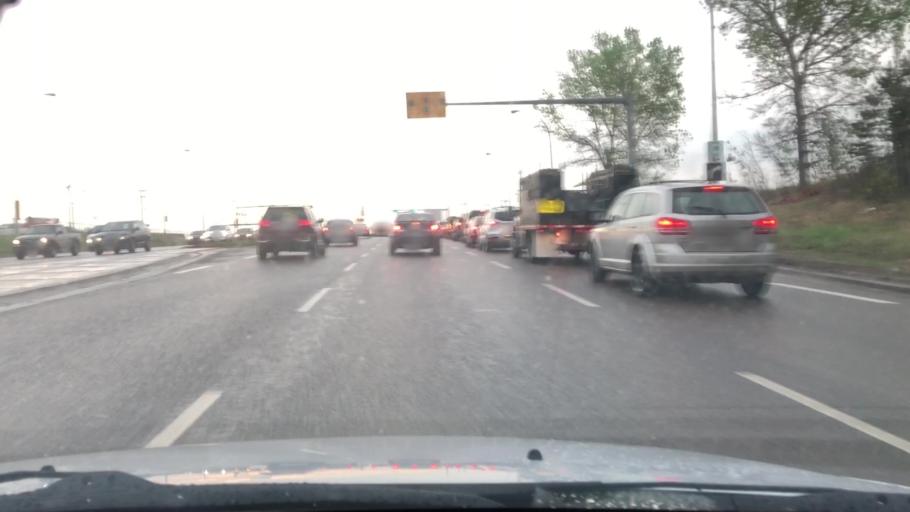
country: CA
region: Alberta
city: Edmonton
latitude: 53.5807
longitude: -113.5281
